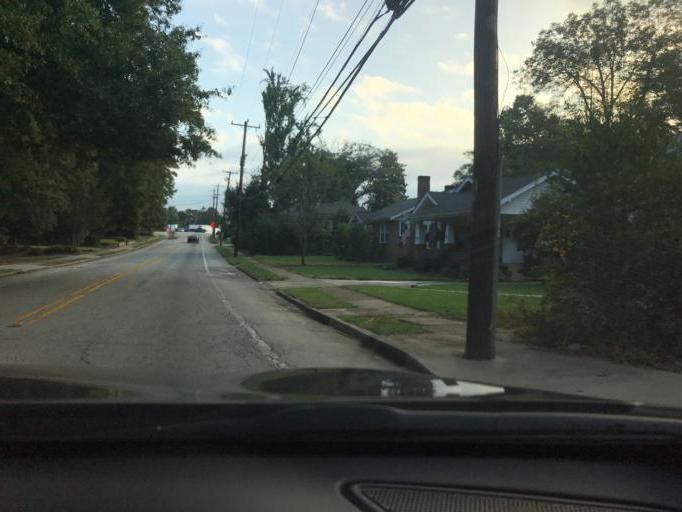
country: US
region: South Carolina
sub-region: Greenville County
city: Dunean
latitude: 34.8224
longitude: -82.3957
